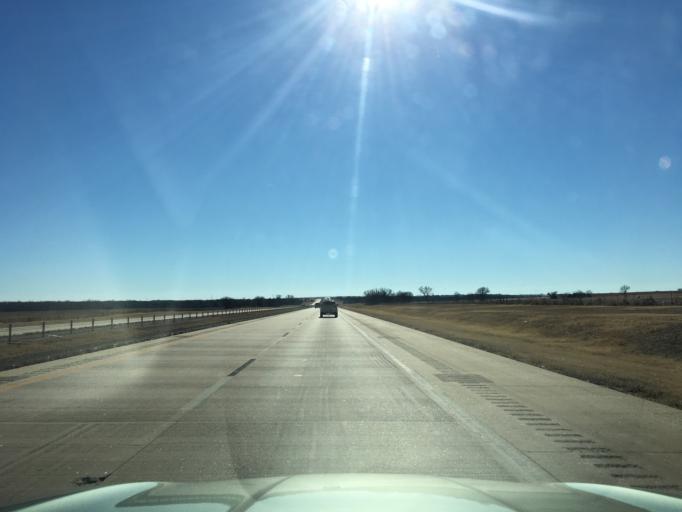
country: US
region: Oklahoma
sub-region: Noble County
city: Perry
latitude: 36.4468
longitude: -97.3271
